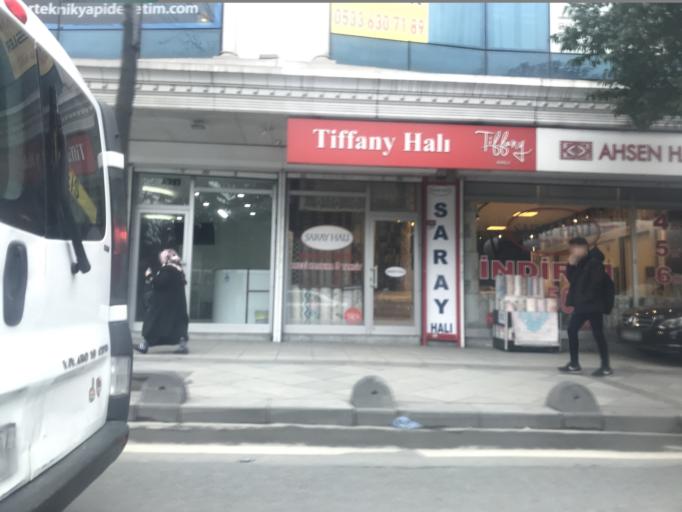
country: TR
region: Istanbul
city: Mahmutbey
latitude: 41.0336
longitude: 28.8336
